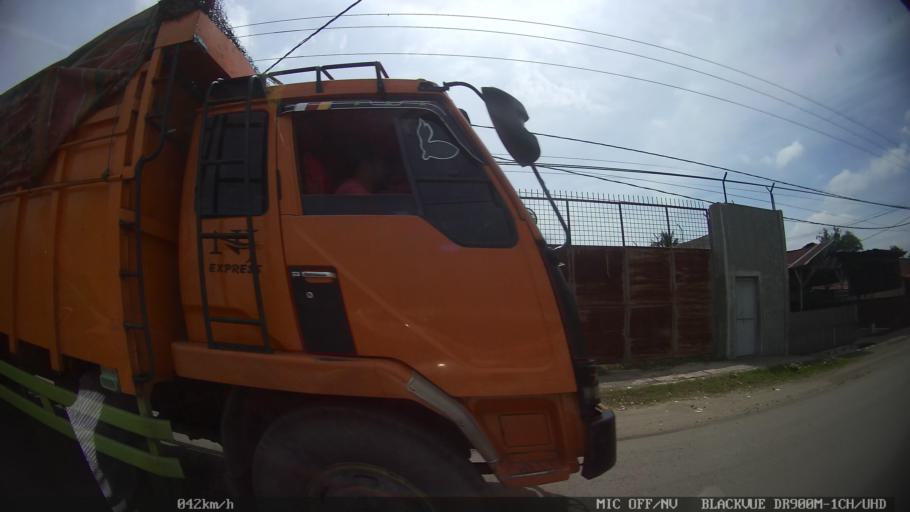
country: ID
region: North Sumatra
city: Medan
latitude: 3.6489
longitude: 98.7170
